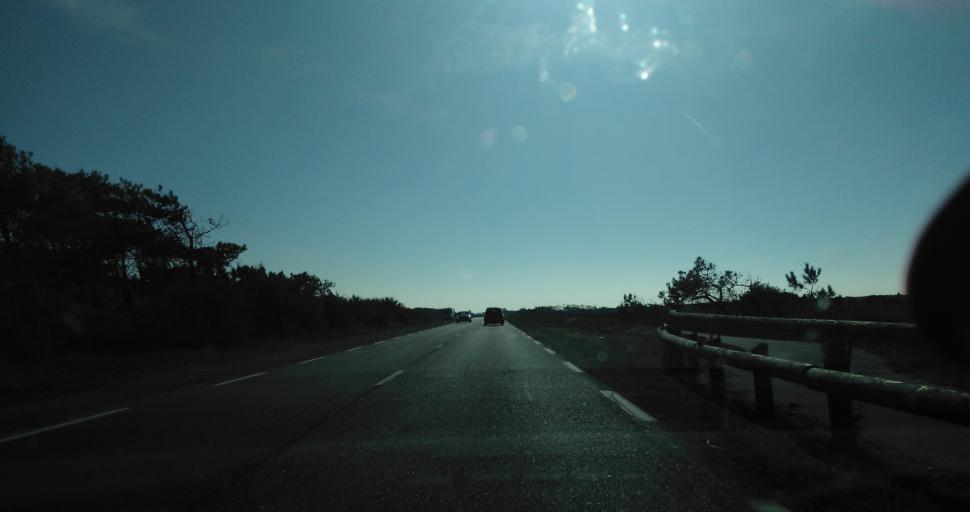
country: FR
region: Brittany
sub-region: Departement du Morbihan
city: Plouharnel
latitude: 47.5861
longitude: -3.1338
